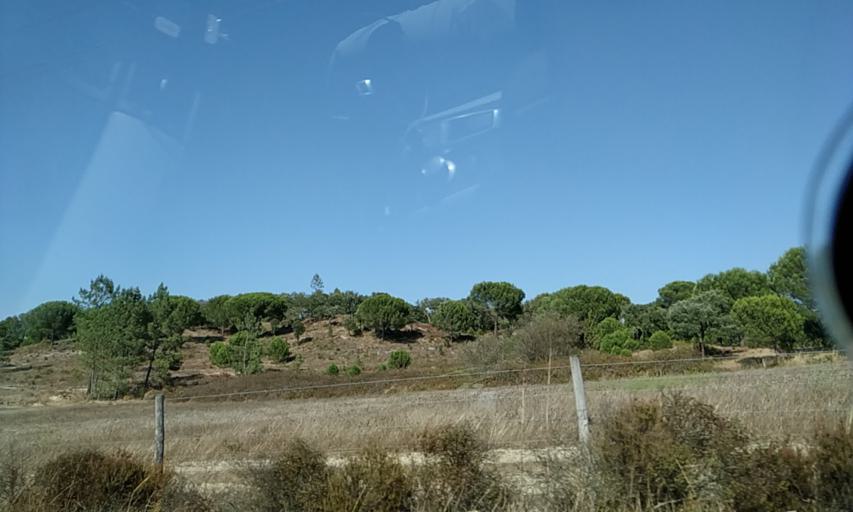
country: PT
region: Santarem
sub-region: Coruche
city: Coruche
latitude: 38.8762
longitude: -8.5397
